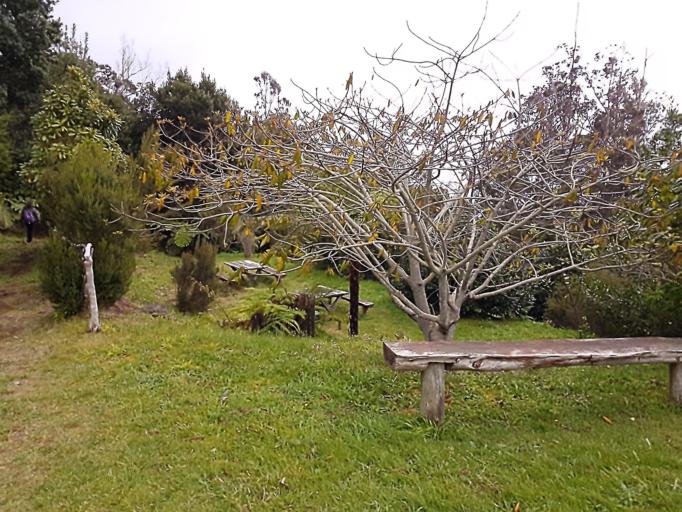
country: PT
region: Madeira
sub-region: Machico
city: Machico
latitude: 32.7483
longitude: -16.7955
